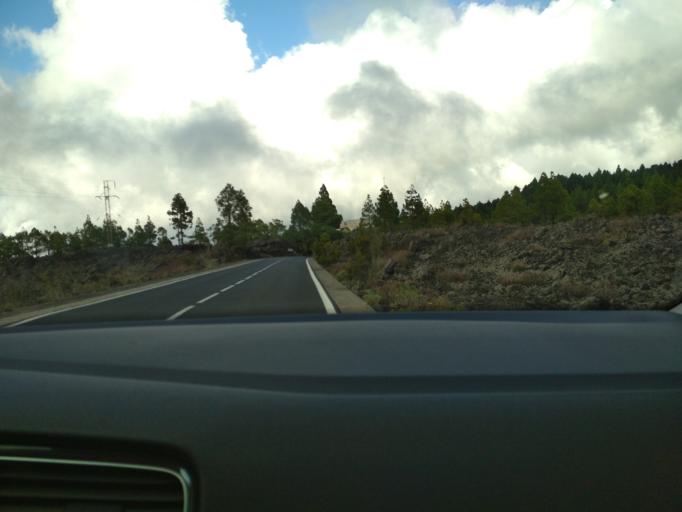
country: ES
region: Canary Islands
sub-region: Provincia de Santa Cruz de Tenerife
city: Garachico
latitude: 28.3312
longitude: -16.7680
